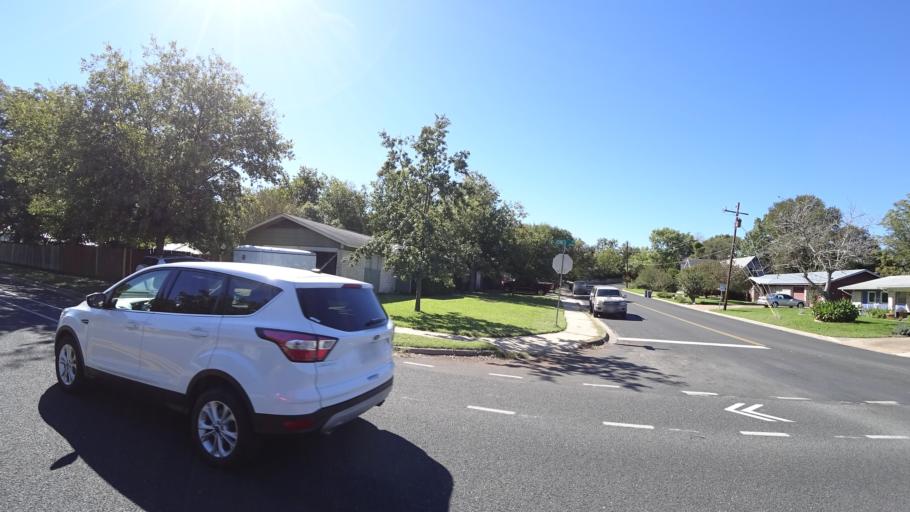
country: US
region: Texas
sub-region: Travis County
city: Rollingwood
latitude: 30.2230
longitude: -97.7986
